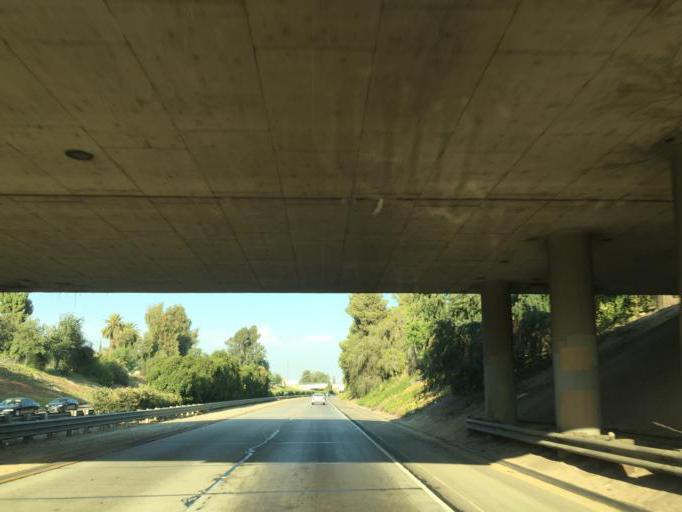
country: US
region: California
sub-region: Tulare County
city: Visalia
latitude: 36.3268
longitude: -119.2836
